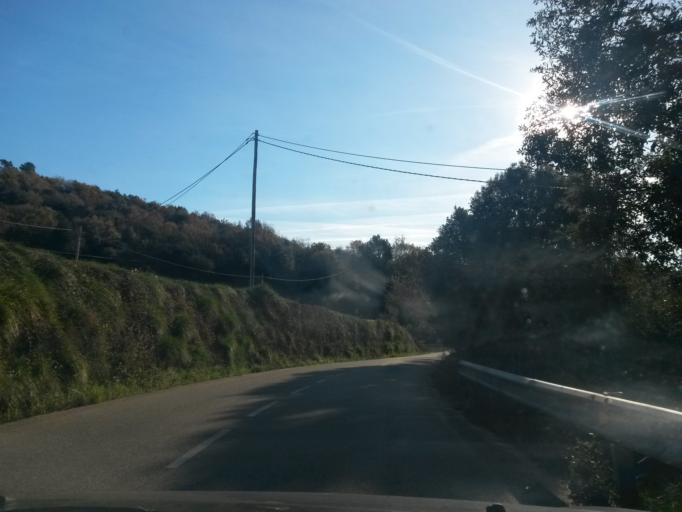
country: ES
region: Catalonia
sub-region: Provincia de Girona
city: la Cellera de Ter
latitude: 41.9687
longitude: 2.6313
